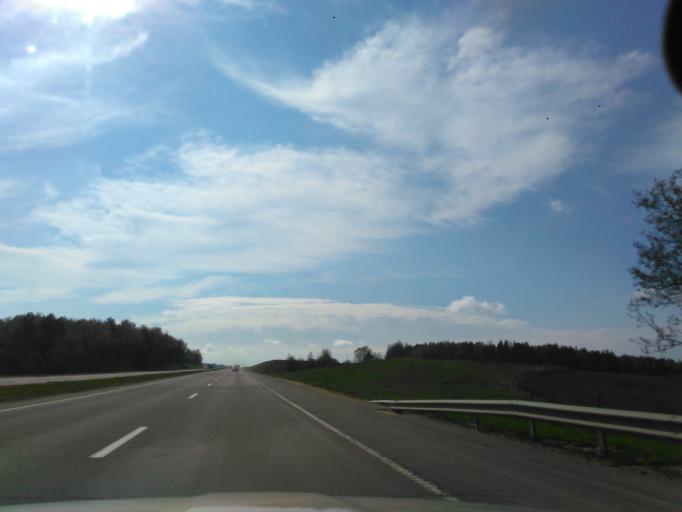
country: BY
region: Minsk
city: Novosel'ye
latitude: 53.9363
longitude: 27.1382
